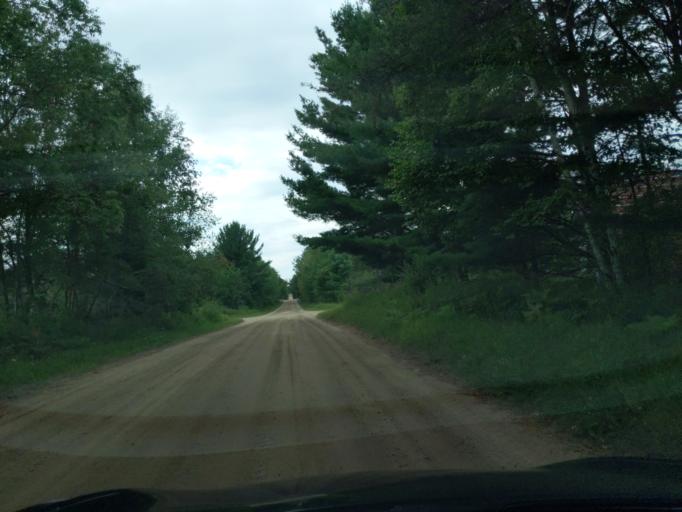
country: US
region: Michigan
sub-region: Clare County
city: Harrison
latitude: 44.0023
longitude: -85.0075
